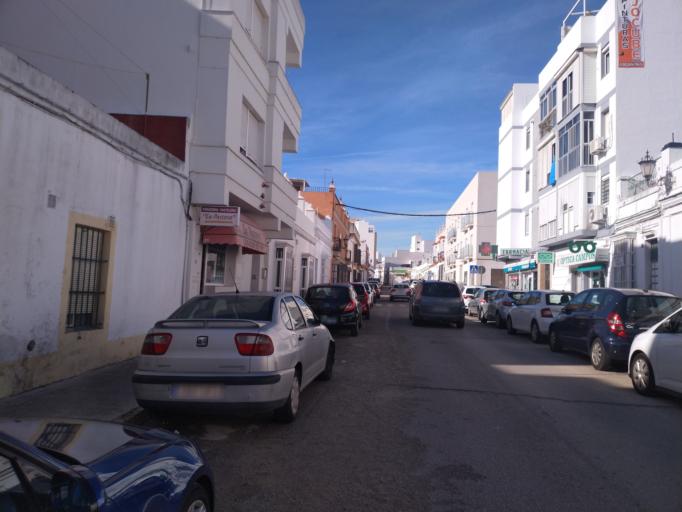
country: ES
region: Andalusia
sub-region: Provincia de Cadiz
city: San Fernando
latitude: 36.4694
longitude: -6.1924
